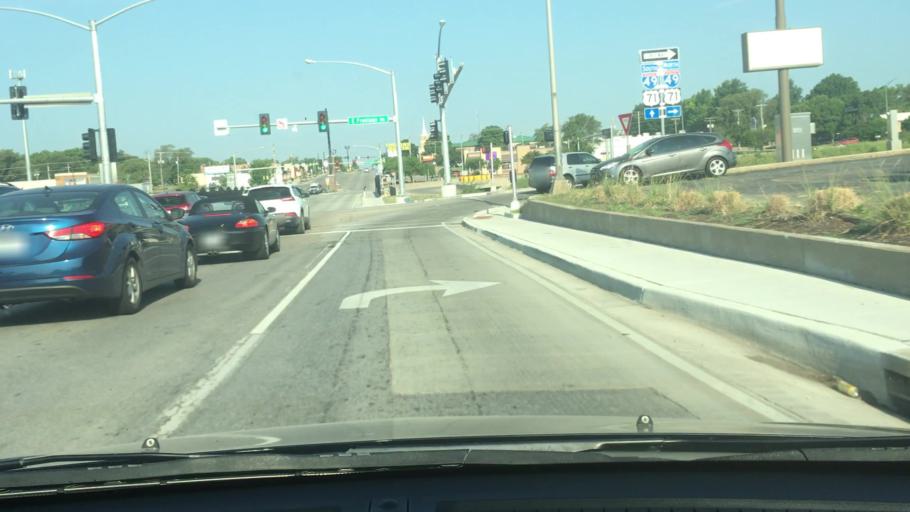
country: US
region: Missouri
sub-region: Jackson County
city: Grandview
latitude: 38.8889
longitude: -94.5237
